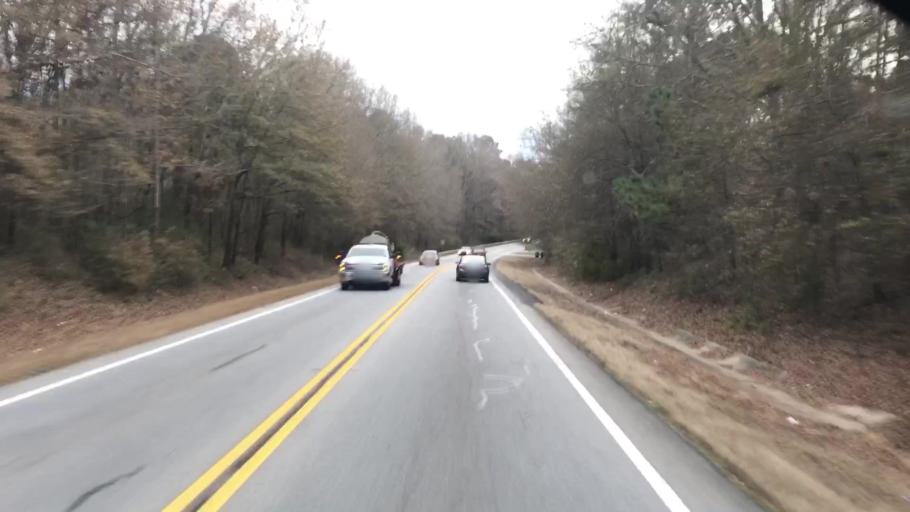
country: US
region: Georgia
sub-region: Barrow County
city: Auburn
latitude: 34.0375
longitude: -83.7747
